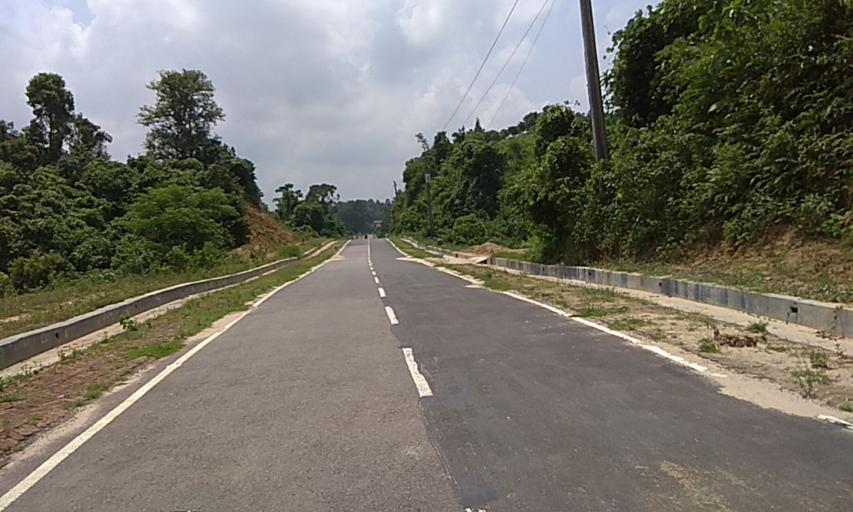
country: BD
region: Chittagong
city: Manikchari
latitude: 22.9371
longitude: 91.9061
